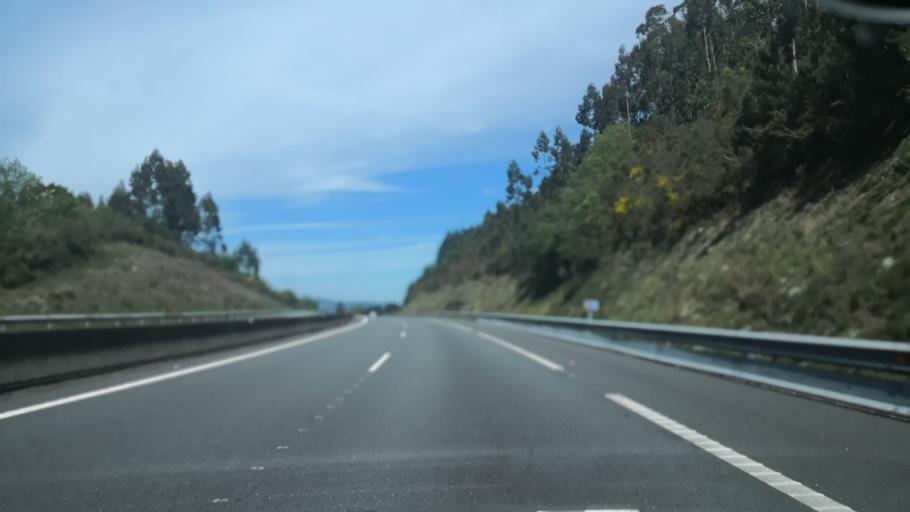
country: ES
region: Galicia
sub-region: Provincia da Coruna
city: Padron
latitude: 42.7662
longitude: -8.6439
